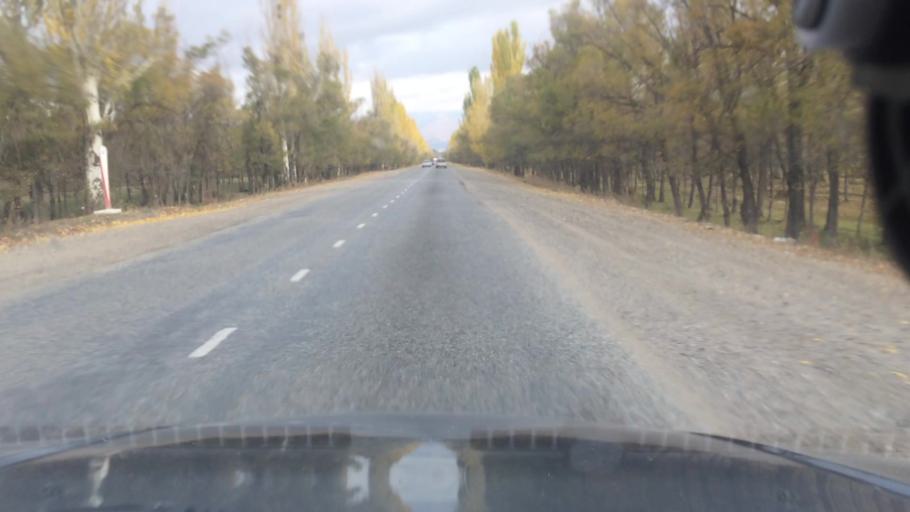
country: KG
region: Ysyk-Koel
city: Tyup
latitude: 42.6333
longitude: 78.3598
